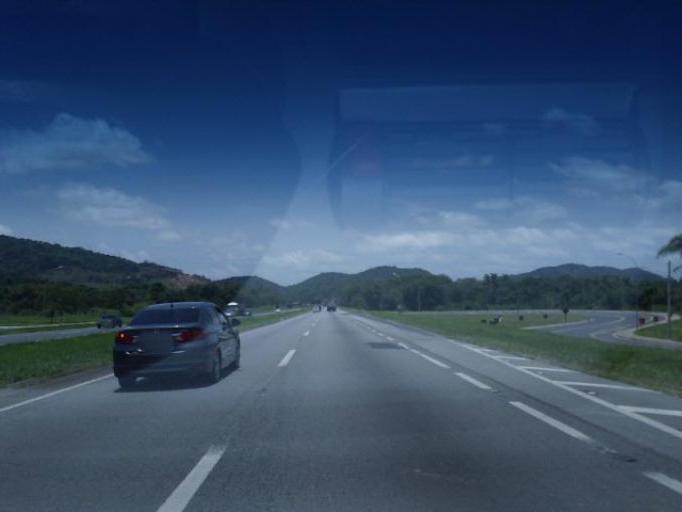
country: BR
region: Sao Paulo
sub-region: Juquia
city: Juquia
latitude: -24.3412
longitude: -47.6460
